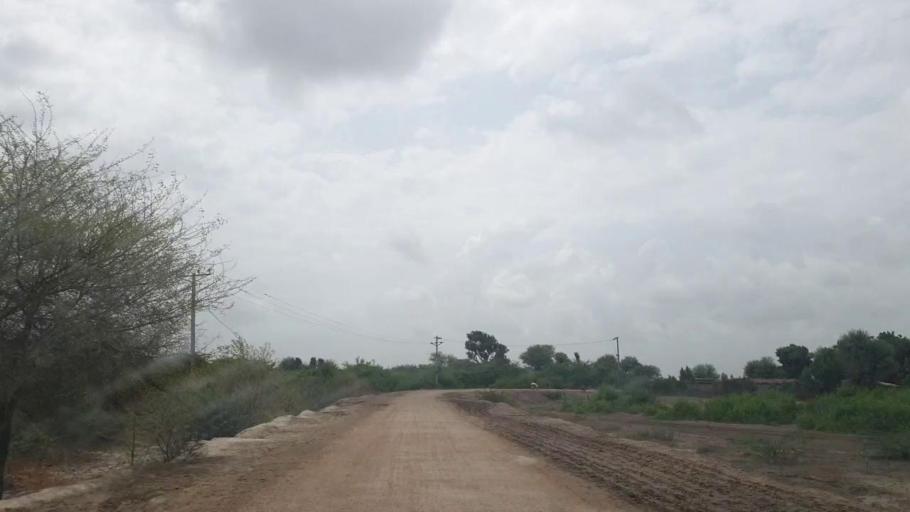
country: PK
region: Sindh
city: Naukot
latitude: 24.9423
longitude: 69.2590
